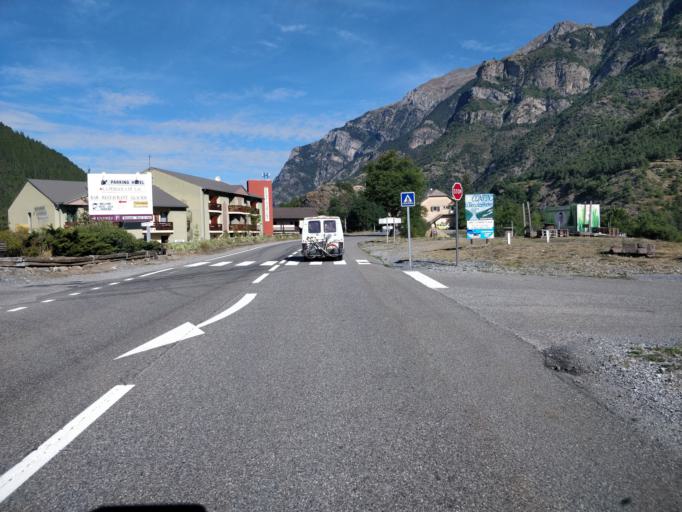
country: FR
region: Provence-Alpes-Cote d'Azur
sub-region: Departement des Alpes-de-Haute-Provence
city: Seyne-les-Alpes
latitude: 44.4257
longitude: 6.4376
